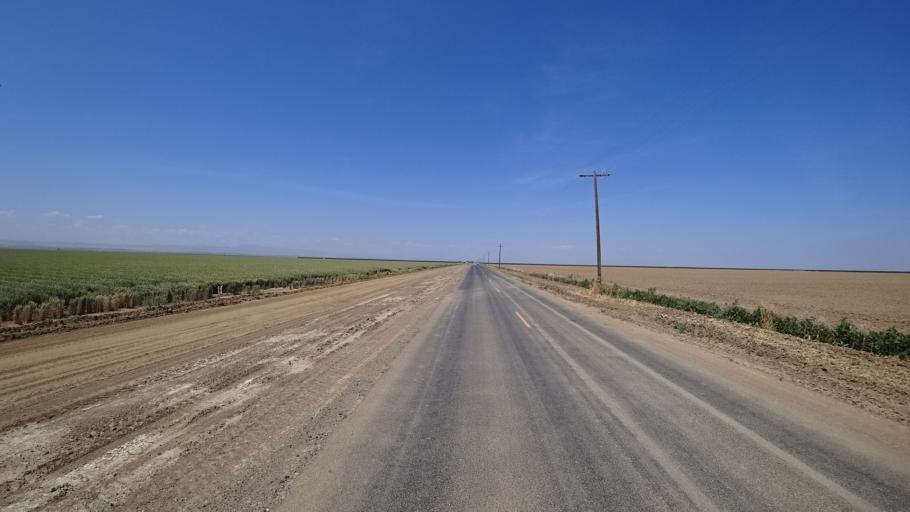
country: US
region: California
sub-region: Kings County
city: Stratford
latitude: 36.1377
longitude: -119.9420
